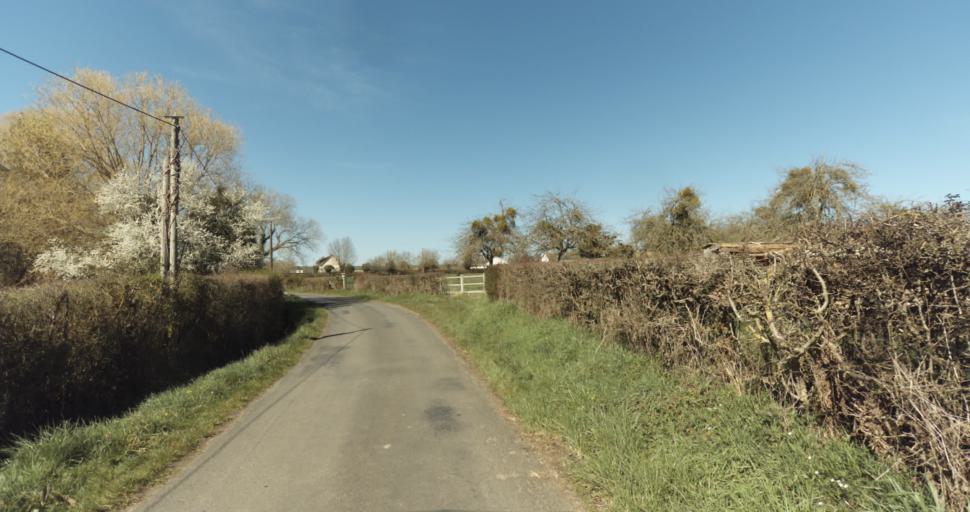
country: FR
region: Lower Normandy
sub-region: Departement du Calvados
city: Saint-Pierre-sur-Dives
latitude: 49.0621
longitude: -0.0276
